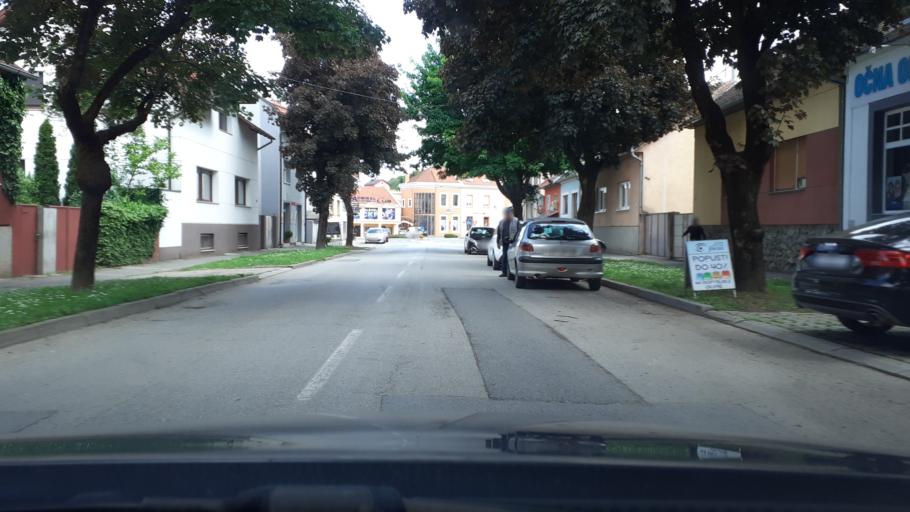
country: HR
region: Pozesko-Slavonska
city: Pozega
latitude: 45.3342
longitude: 17.6823
